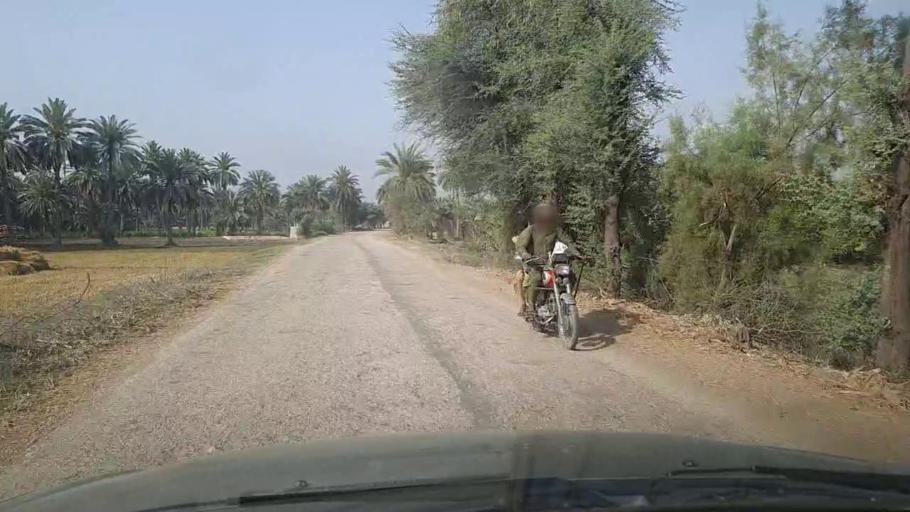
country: PK
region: Sindh
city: Pir jo Goth
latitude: 27.5449
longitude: 68.5251
